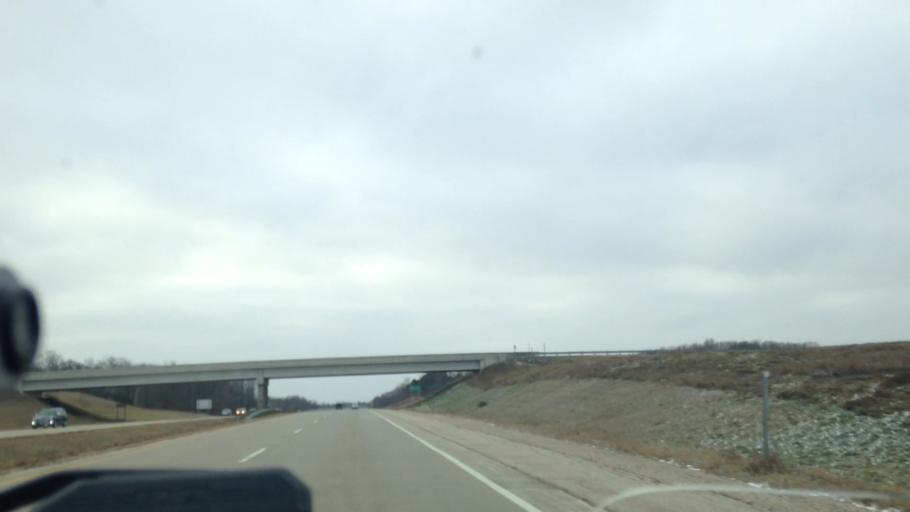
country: US
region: Wisconsin
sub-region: Washington County
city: West Bend
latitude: 43.3847
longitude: -88.1929
